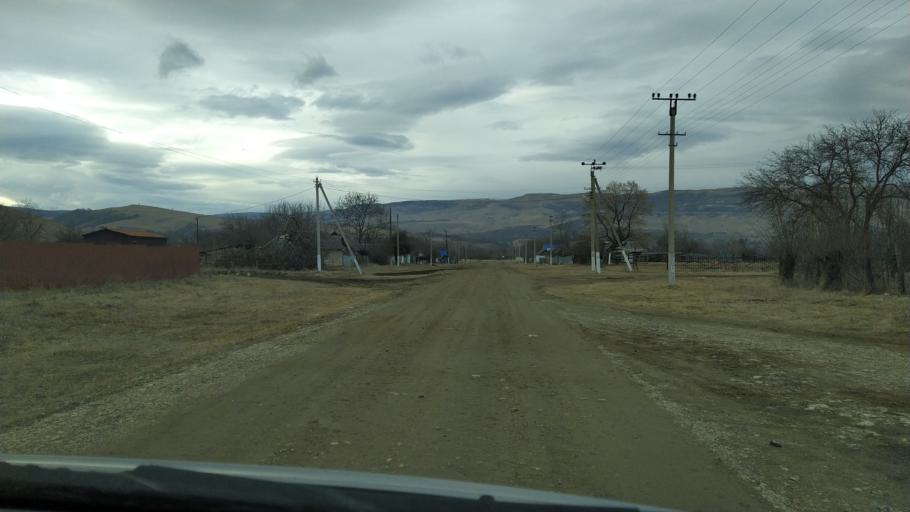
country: RU
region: Krasnodarskiy
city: Peredovaya
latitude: 44.0817
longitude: 41.3698
